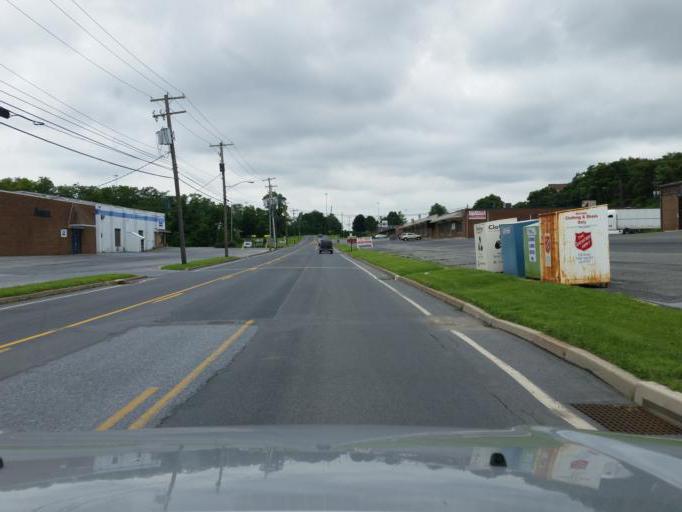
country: US
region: Pennsylvania
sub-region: Dauphin County
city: Rutherford
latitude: 40.2665
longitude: -76.7570
